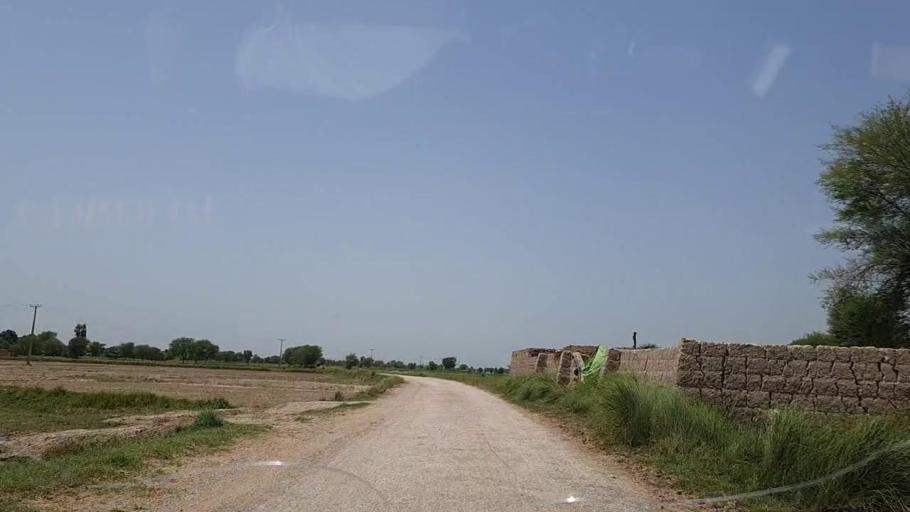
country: PK
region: Sindh
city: Tharu Shah
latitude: 26.9262
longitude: 68.0555
